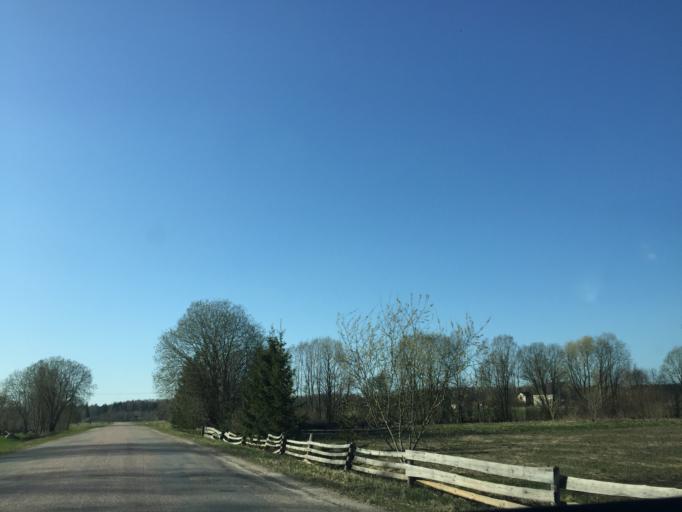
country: LV
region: Ropazu
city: Ropazi
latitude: 56.9638
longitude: 24.6846
